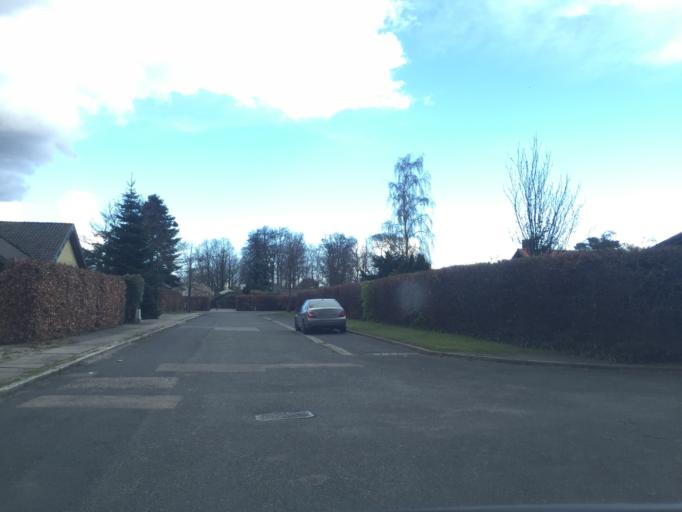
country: DK
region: Capital Region
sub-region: Gentofte Kommune
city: Charlottenlund
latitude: 55.7630
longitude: 12.5691
